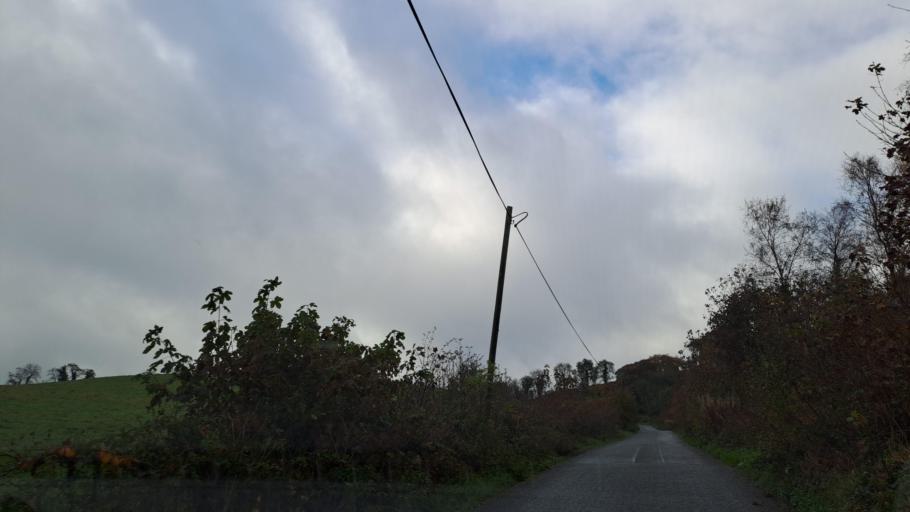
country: IE
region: Ulster
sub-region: An Cabhan
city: Bailieborough
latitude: 53.9593
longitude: -6.9869
